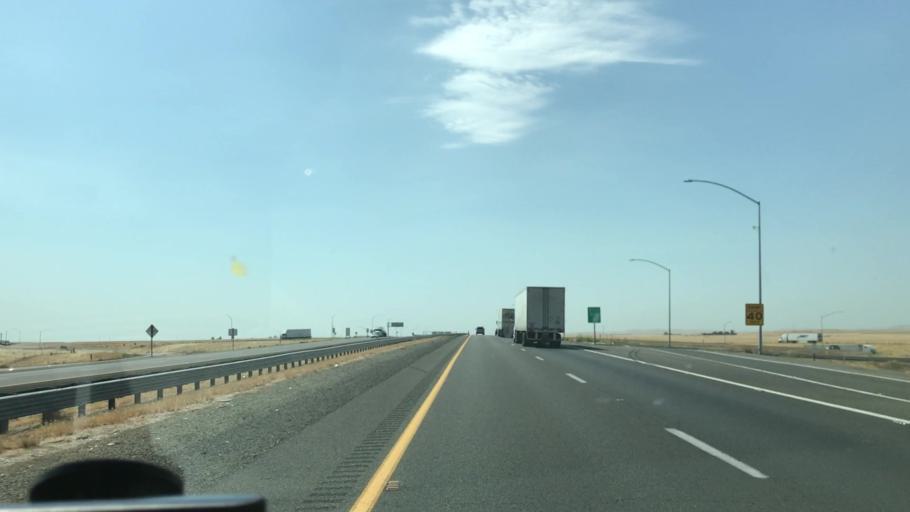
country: US
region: California
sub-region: Merced County
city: Los Banos
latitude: 37.0594
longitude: -120.9726
